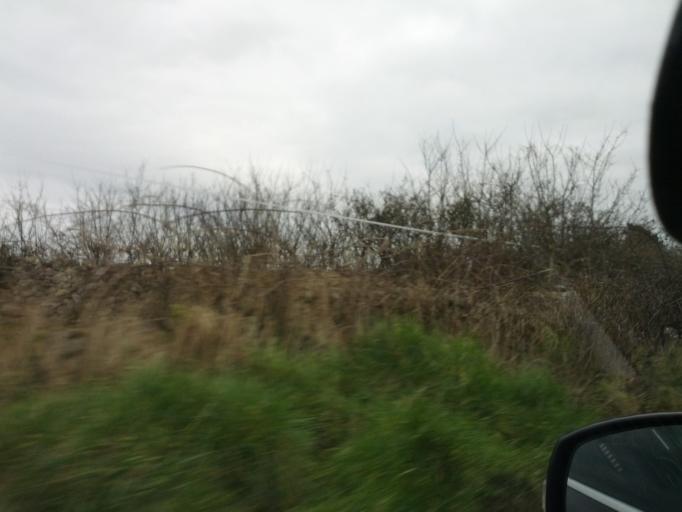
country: IE
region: Connaught
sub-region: County Galway
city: Athenry
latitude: 53.2693
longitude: -8.7430
